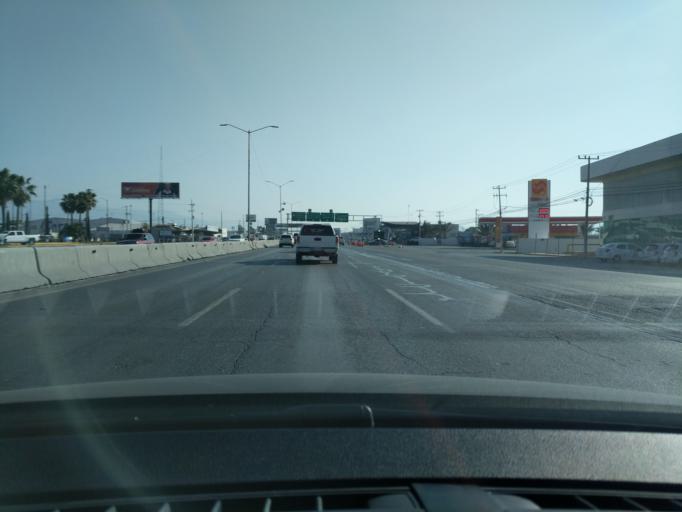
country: MX
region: Coahuila
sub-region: Ramos Arizpe
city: Ramos Arizpe
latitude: 25.4952
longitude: -100.9662
